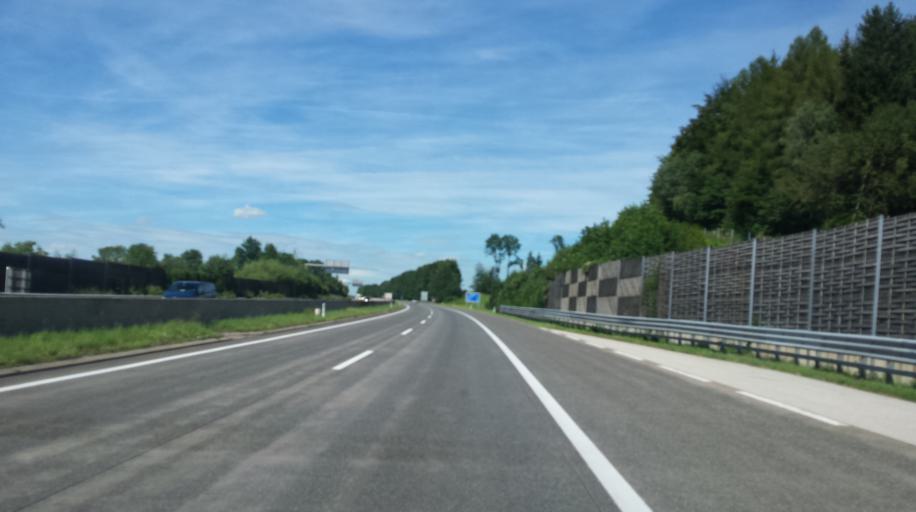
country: AT
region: Upper Austria
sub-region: Politischer Bezirk Vocklabruck
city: Attersee
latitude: 47.9339
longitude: 13.5140
